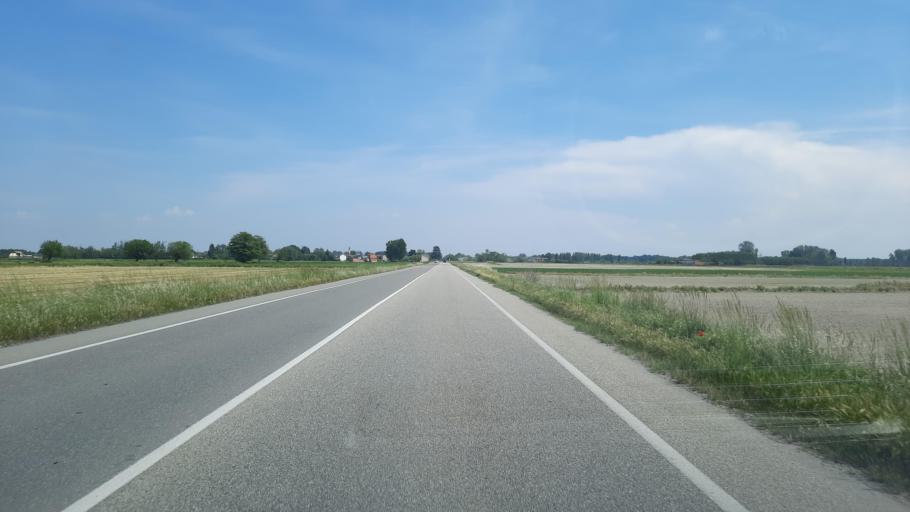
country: IT
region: Lombardy
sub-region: Provincia di Pavia
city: Mortara
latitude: 45.2427
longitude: 8.7760
